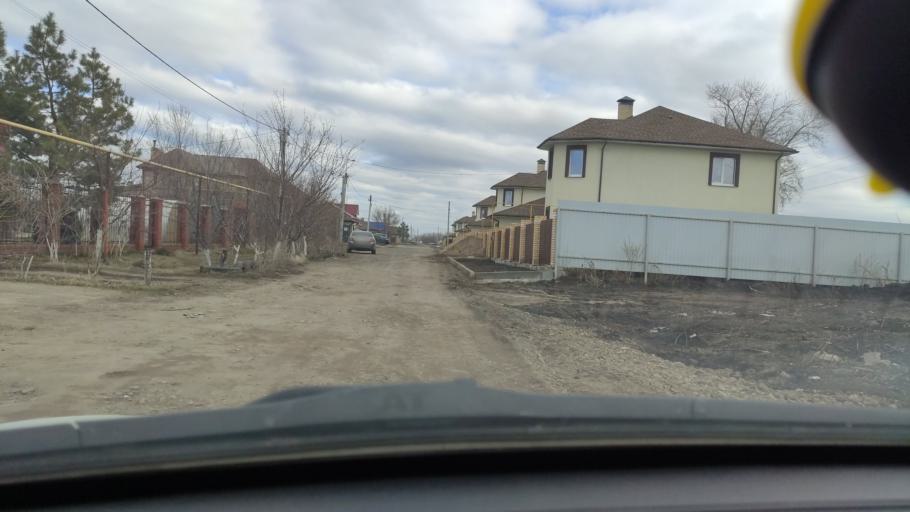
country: RU
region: Samara
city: Tol'yatti
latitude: 53.5498
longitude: 49.4003
